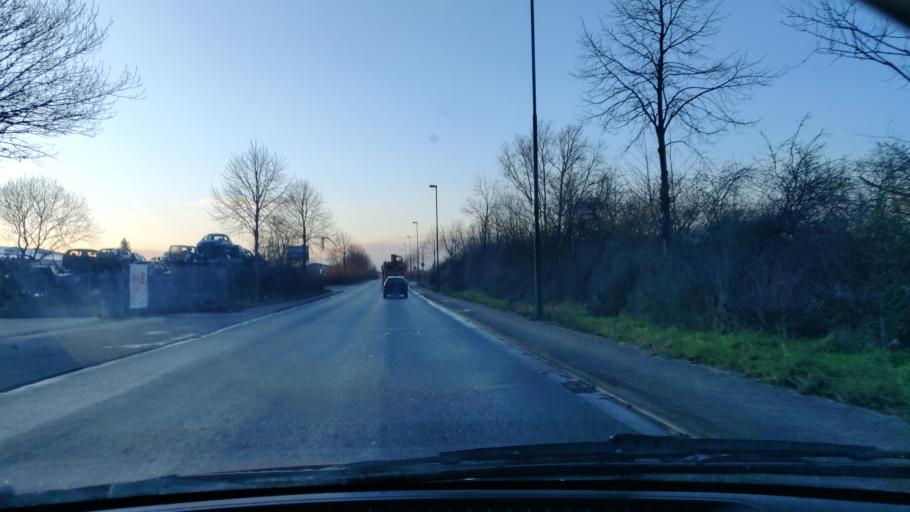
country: DE
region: North Rhine-Westphalia
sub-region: Regierungsbezirk Koln
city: Kerpen
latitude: 50.8966
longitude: 6.6530
